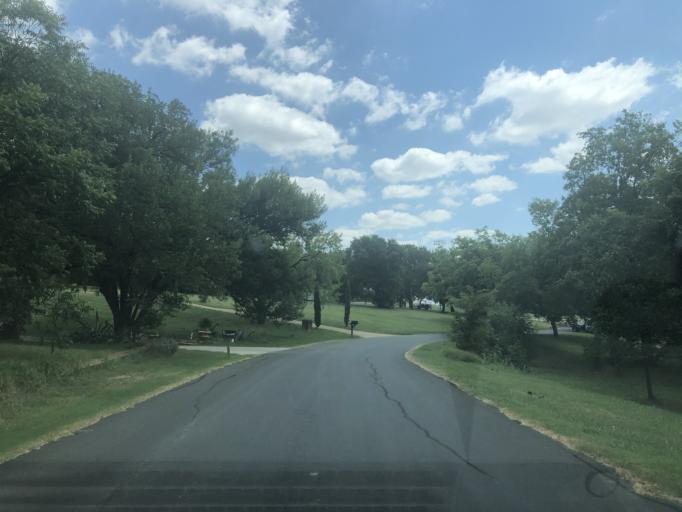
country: US
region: Texas
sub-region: Dallas County
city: Grand Prairie
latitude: 32.7515
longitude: -97.0074
